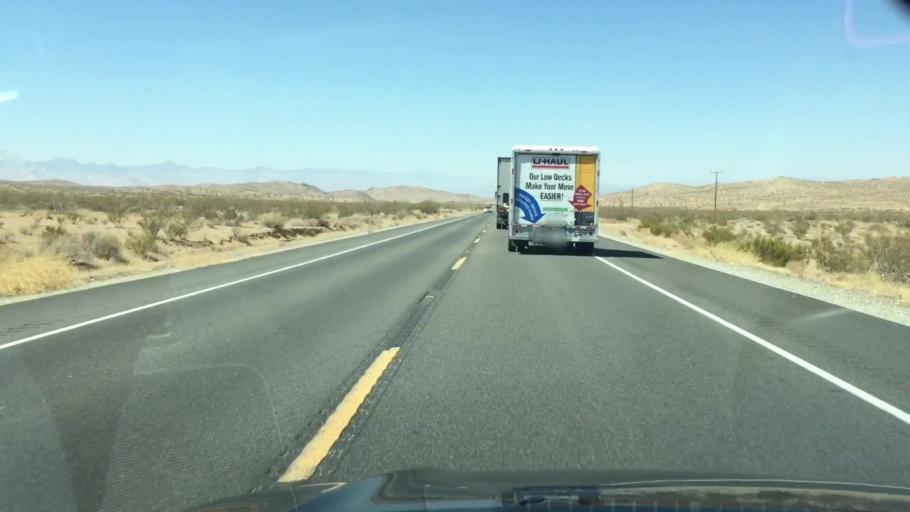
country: US
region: California
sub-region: Kern County
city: Ridgecrest
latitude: 35.5077
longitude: -117.6675
